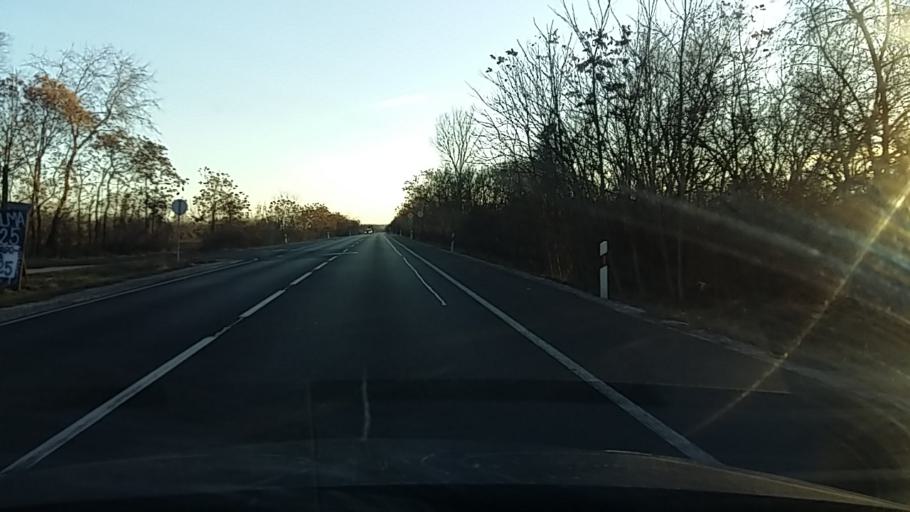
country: HU
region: Szabolcs-Szatmar-Bereg
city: Ujfeherto
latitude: 47.8633
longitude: 21.7046
